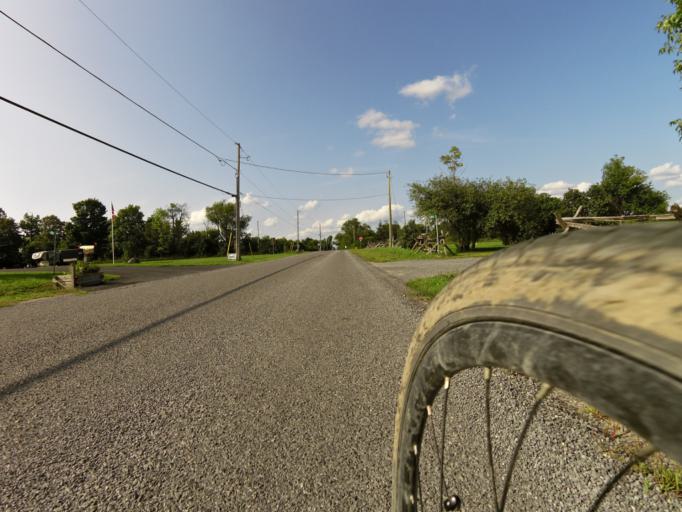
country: CA
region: Ontario
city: Kingston
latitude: 44.3810
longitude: -76.5955
